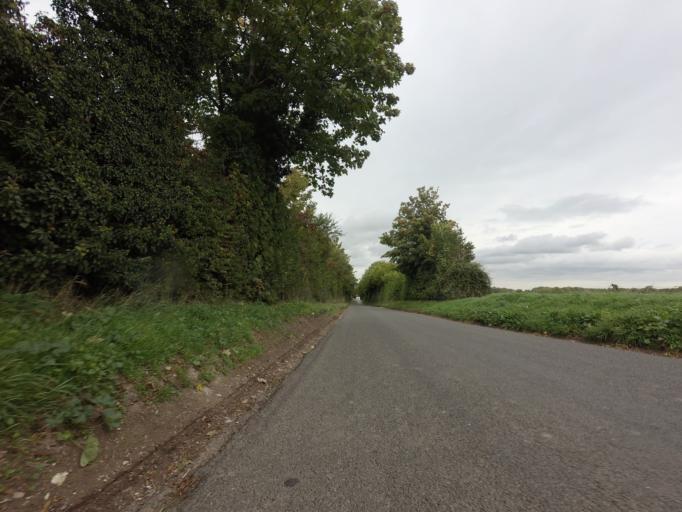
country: GB
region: England
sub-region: Cambridgeshire
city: Duxford
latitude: 52.0611
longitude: 0.1049
